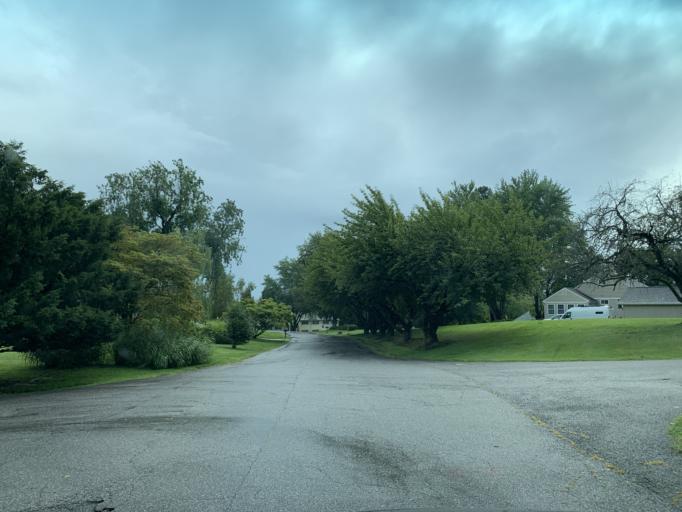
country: US
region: Maryland
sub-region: Baltimore County
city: Timonium
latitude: 39.4481
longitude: -76.6250
